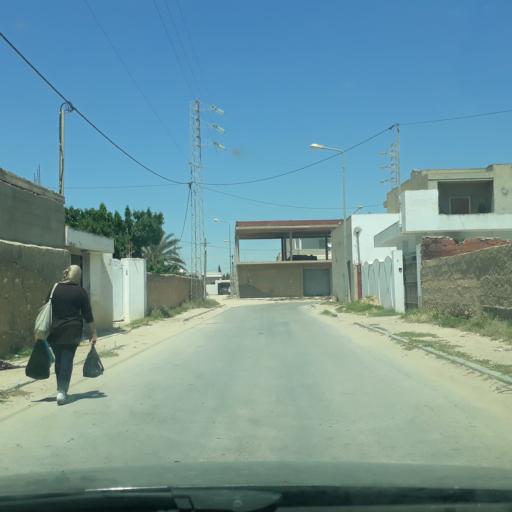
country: TN
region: Safaqis
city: Al Qarmadah
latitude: 34.8151
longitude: 10.7573
